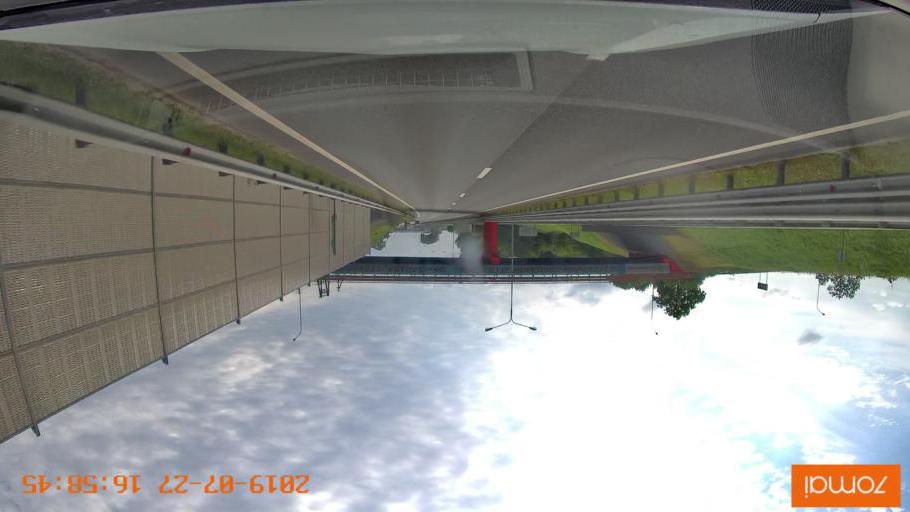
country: RU
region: Kaliningrad
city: Bol'shoe Isakovo
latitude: 54.7015
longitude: 20.6708
